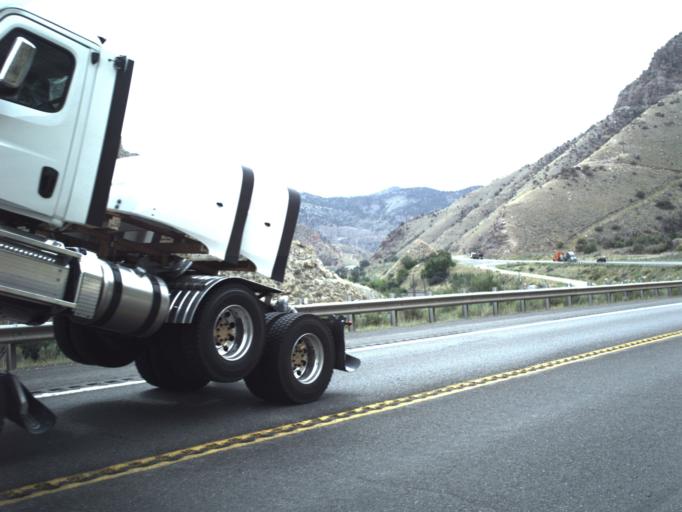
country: US
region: Utah
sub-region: Carbon County
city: Helper
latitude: 39.7496
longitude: -110.8850
